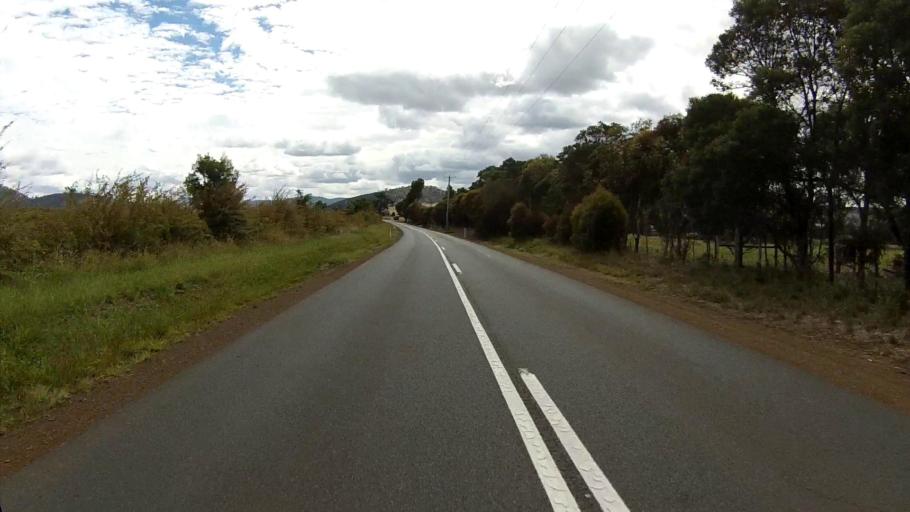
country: AU
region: Tasmania
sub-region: Clarence
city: Cambridge
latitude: -42.7601
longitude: 147.4005
